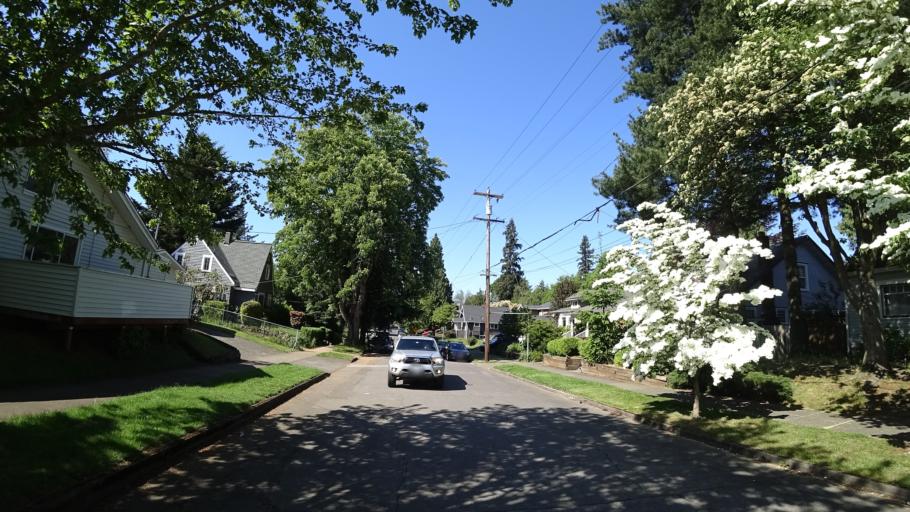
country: US
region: Oregon
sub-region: Clackamas County
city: Milwaukie
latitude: 45.4822
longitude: -122.6175
